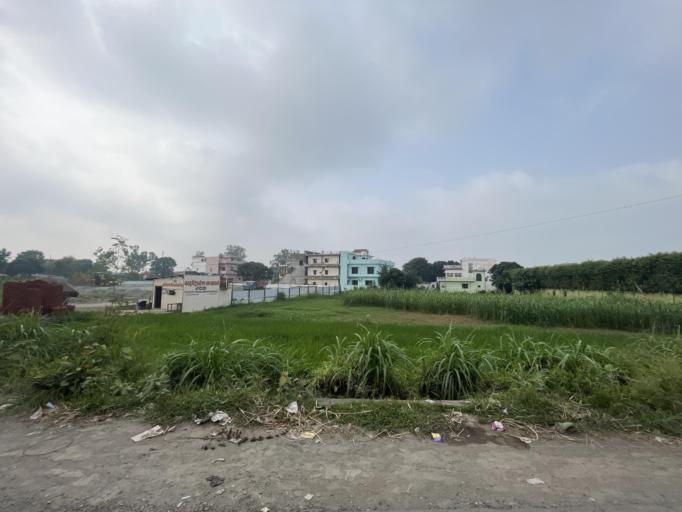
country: IN
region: Uttarakhand
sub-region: Naini Tal
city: Haldwani
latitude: 29.1941
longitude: 79.5067
